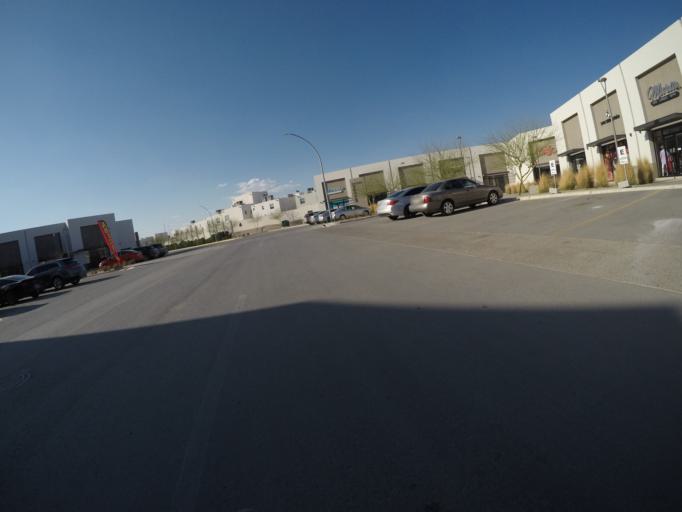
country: US
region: Texas
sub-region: El Paso County
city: Socorro
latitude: 31.7004
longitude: -106.3886
